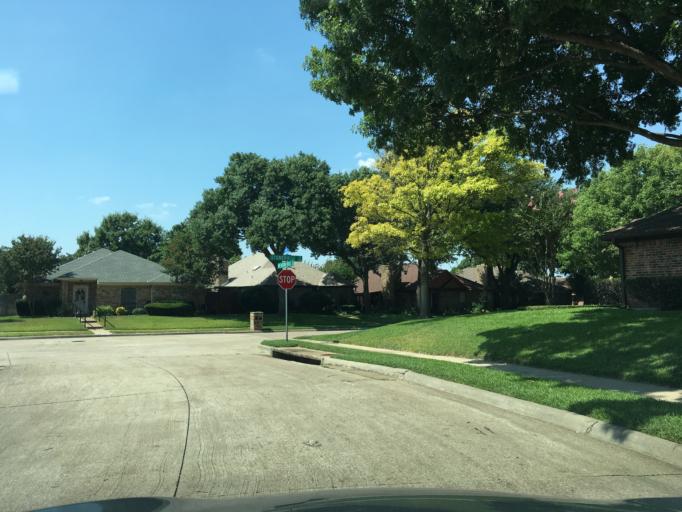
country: US
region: Texas
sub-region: Dallas County
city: Garland
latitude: 32.9419
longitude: -96.6690
